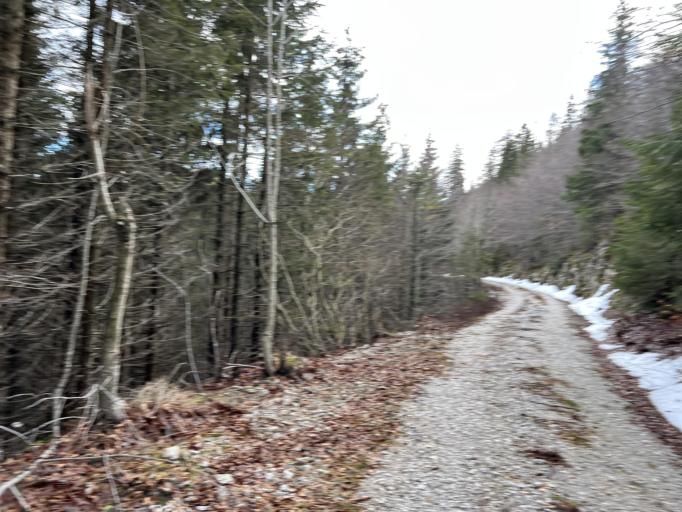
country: SI
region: Nova Gorica
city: Sempas
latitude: 45.9851
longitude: 13.8082
